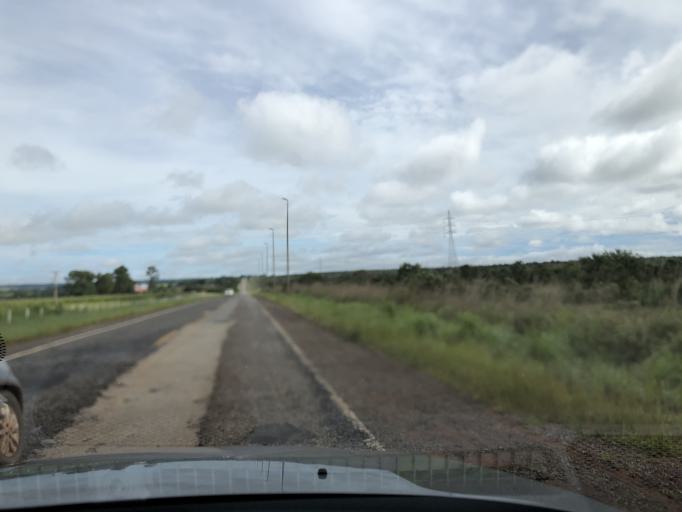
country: BR
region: Federal District
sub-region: Brasilia
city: Brasilia
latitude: -15.7199
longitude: -48.0868
